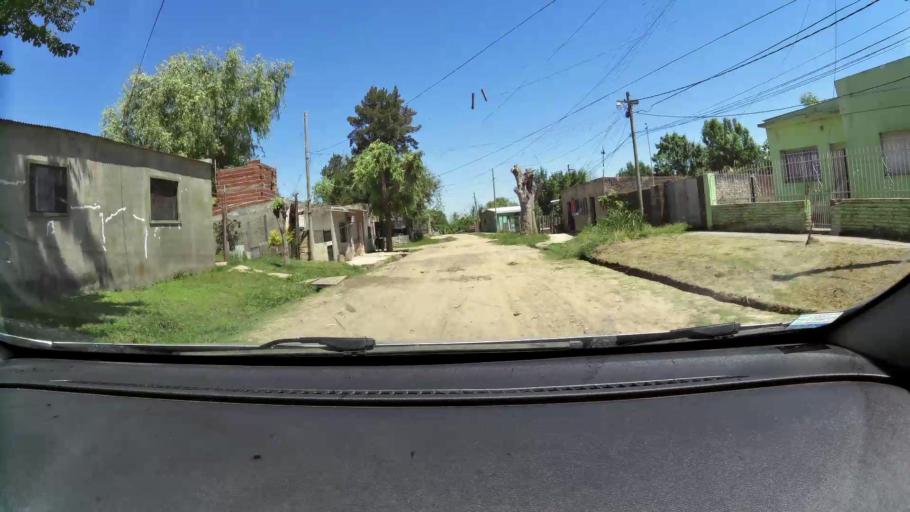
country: AR
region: Santa Fe
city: Santa Fe de la Vera Cruz
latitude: -31.6124
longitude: -60.7194
